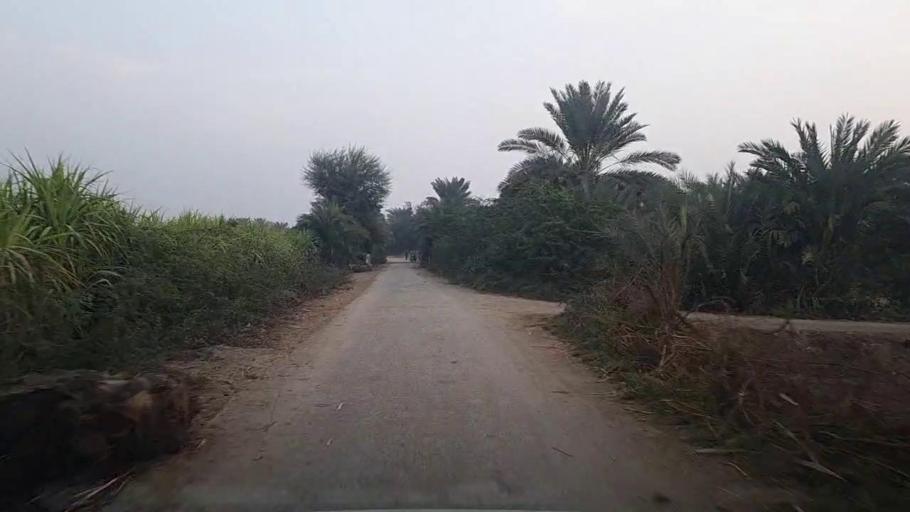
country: PK
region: Sindh
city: Kot Diji
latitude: 27.3360
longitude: 68.6390
